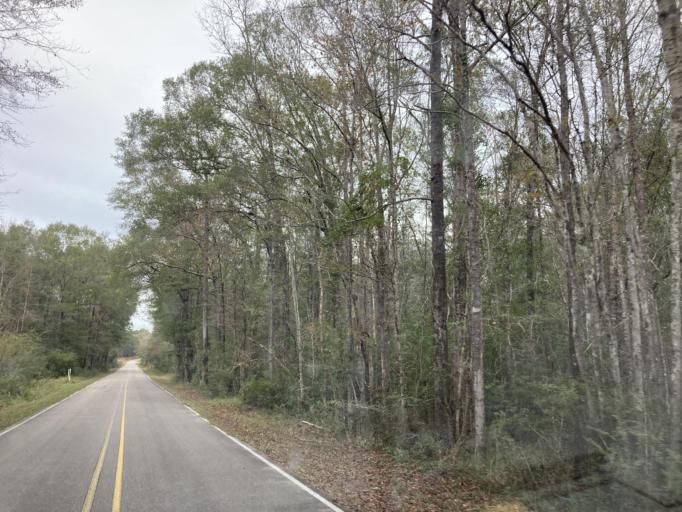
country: US
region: Mississippi
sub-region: Lamar County
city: Lumberton
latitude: 31.0590
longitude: -89.4336
